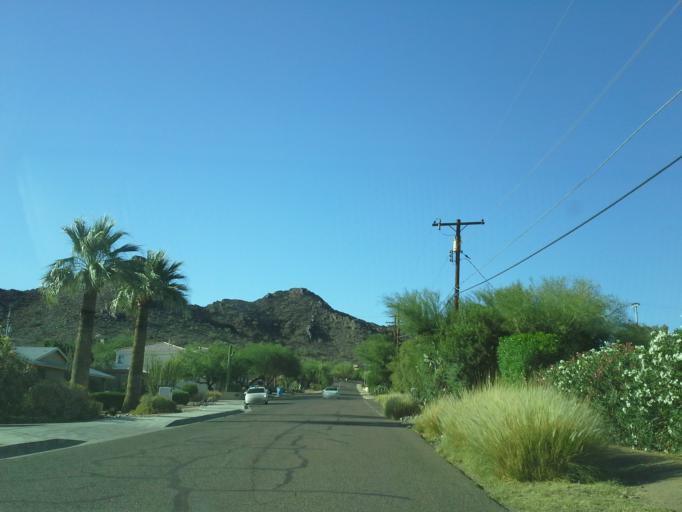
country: US
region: Arizona
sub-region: Maricopa County
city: Paradise Valley
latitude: 33.5580
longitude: -112.0479
